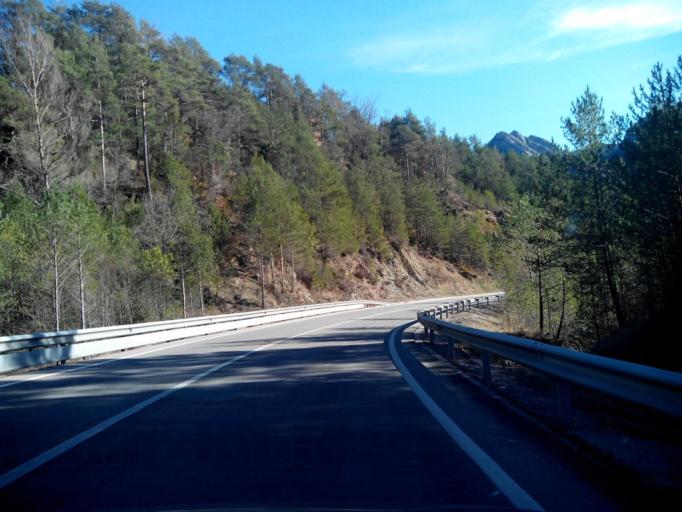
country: ES
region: Catalonia
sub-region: Provincia de Barcelona
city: Vilada
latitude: 42.1317
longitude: 1.9090
